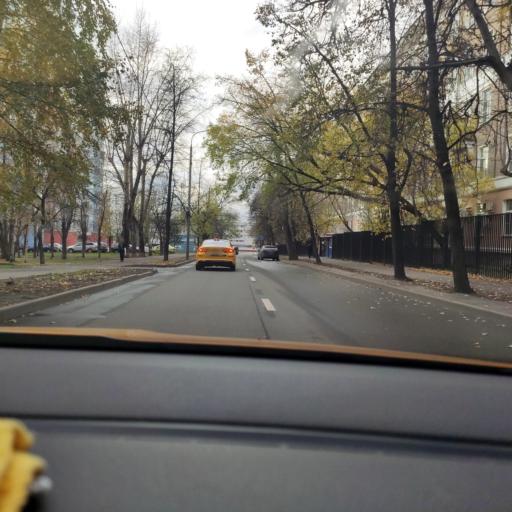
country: RU
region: Moscow
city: Tekstil'shchiki
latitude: 55.6966
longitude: 37.7370
